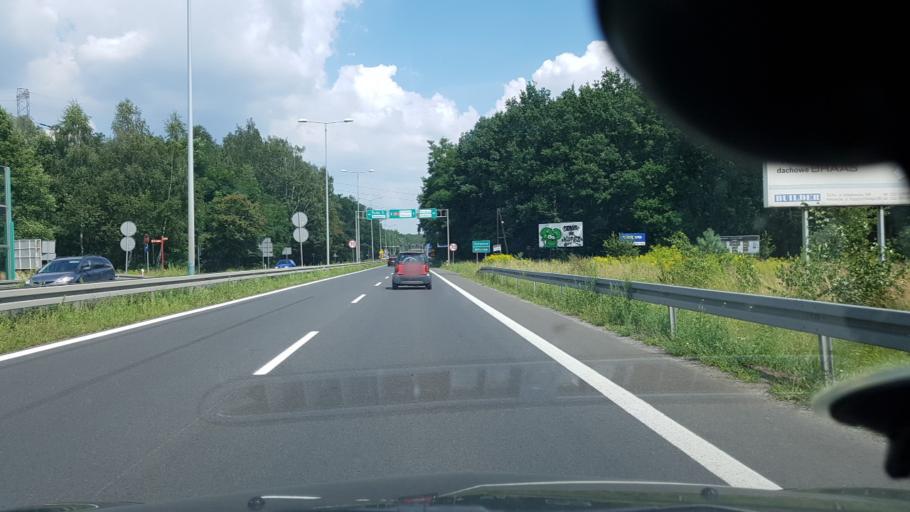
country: PL
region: Silesian Voivodeship
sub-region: Powiat mikolowski
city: Mikolow
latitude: 50.1941
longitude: 18.9286
